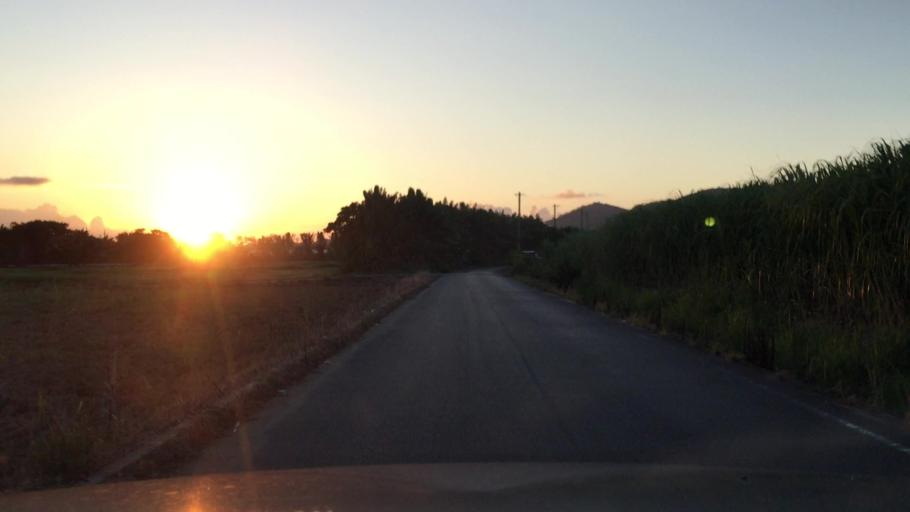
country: JP
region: Okinawa
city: Ishigaki
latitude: 24.3522
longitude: 124.1648
